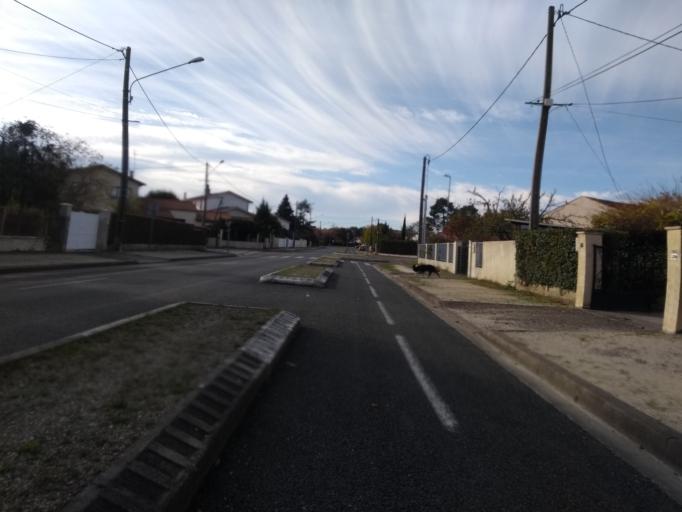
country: FR
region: Aquitaine
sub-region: Departement de la Gironde
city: Pessac
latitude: 44.7988
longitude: -0.6775
